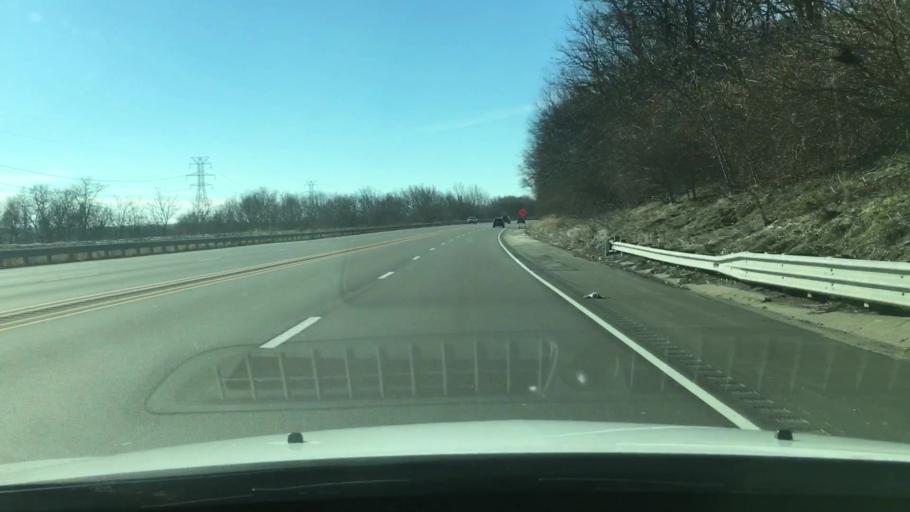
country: US
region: Illinois
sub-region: Tazewell County
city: Pekin
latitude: 40.5951
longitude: -89.6725
